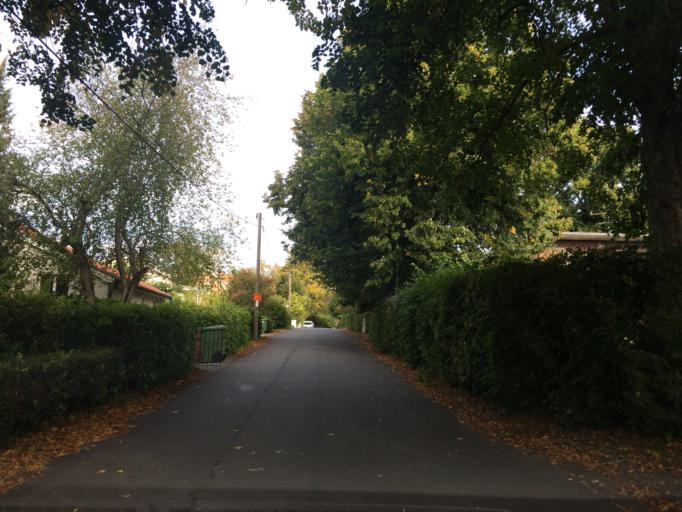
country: SE
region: Stockholm
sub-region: Sollentuna Kommun
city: Sollentuna
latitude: 59.4541
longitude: 17.9292
